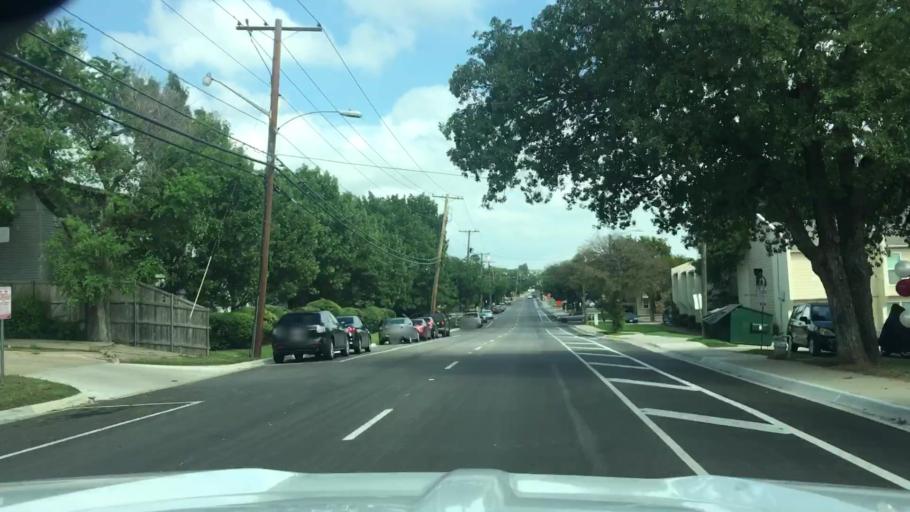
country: US
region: Texas
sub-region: Denton County
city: Denton
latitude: 33.2148
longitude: -97.1592
